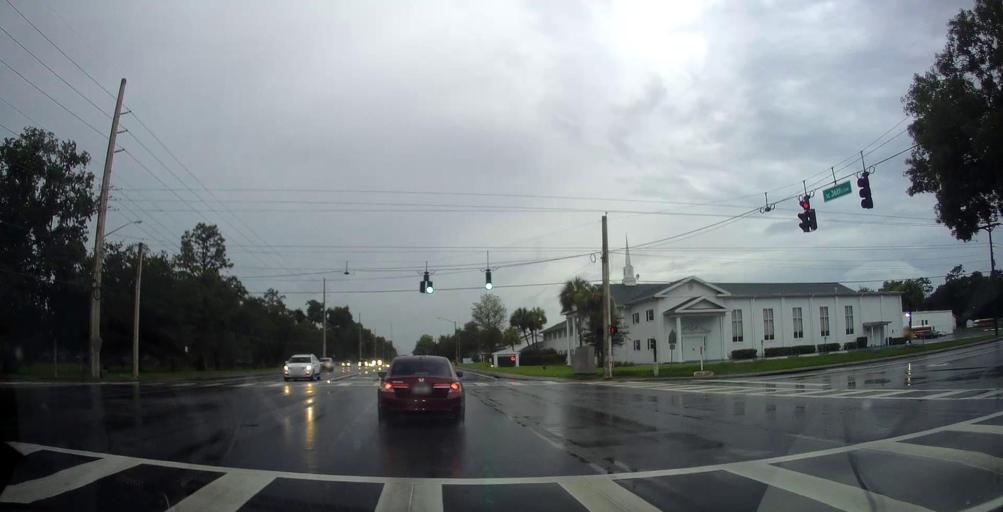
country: US
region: Florida
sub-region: Marion County
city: Ocala
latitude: 29.1719
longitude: -82.0870
